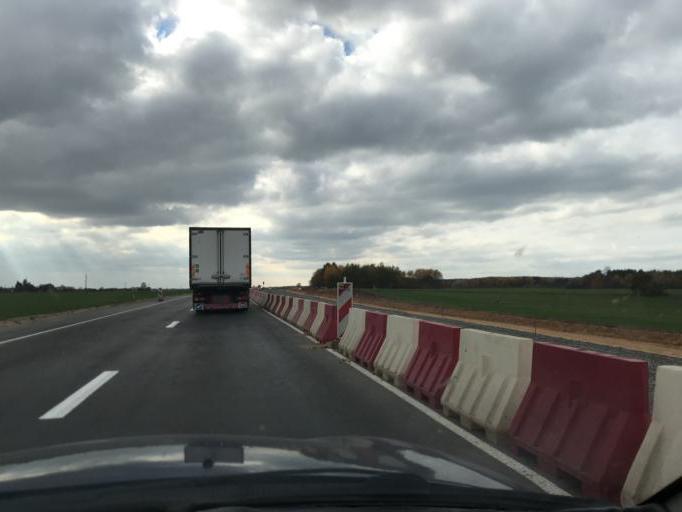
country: BY
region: Grodnenskaya
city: Lida
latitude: 53.8143
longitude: 25.1163
